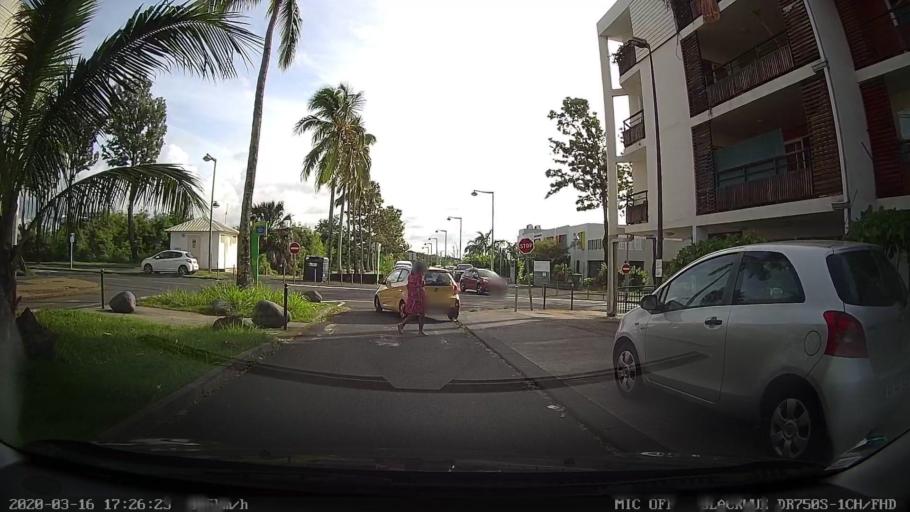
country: RE
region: Reunion
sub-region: Reunion
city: Sainte-Marie
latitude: -20.9069
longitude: 55.4990
